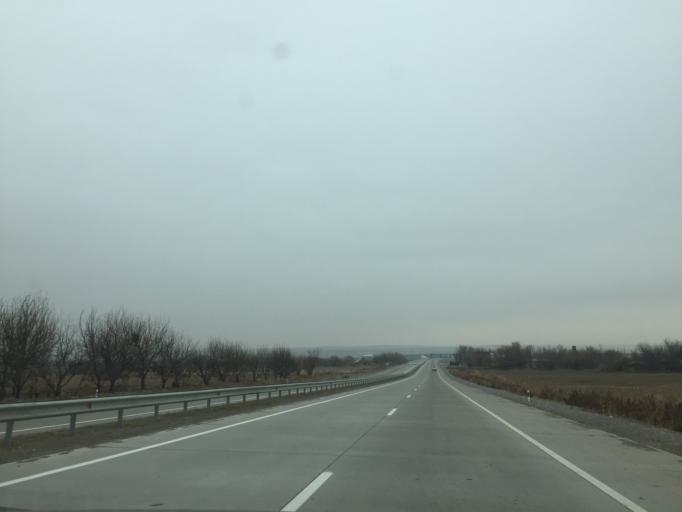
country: KZ
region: Ongtustik Qazaqstan
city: Aksu
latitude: 42.4703
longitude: 69.8020
